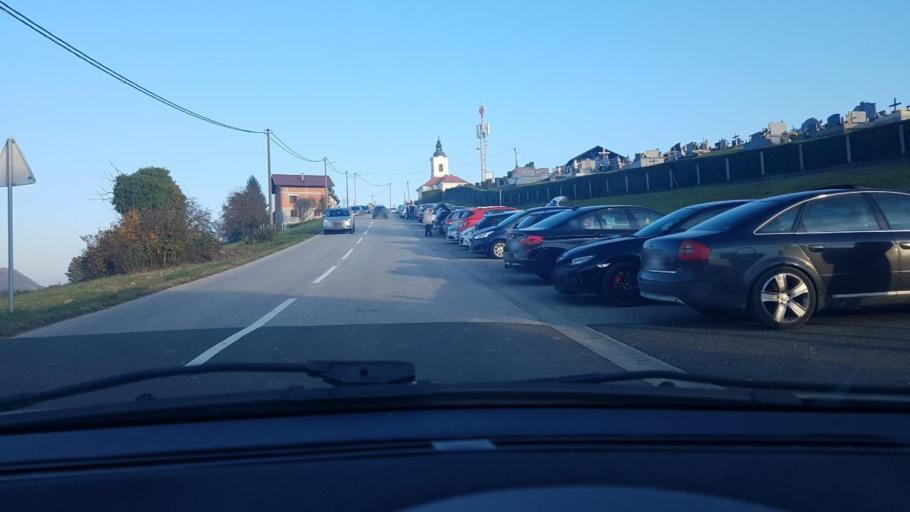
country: SI
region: Rogatec
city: Rogatec
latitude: 46.2139
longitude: 15.6700
